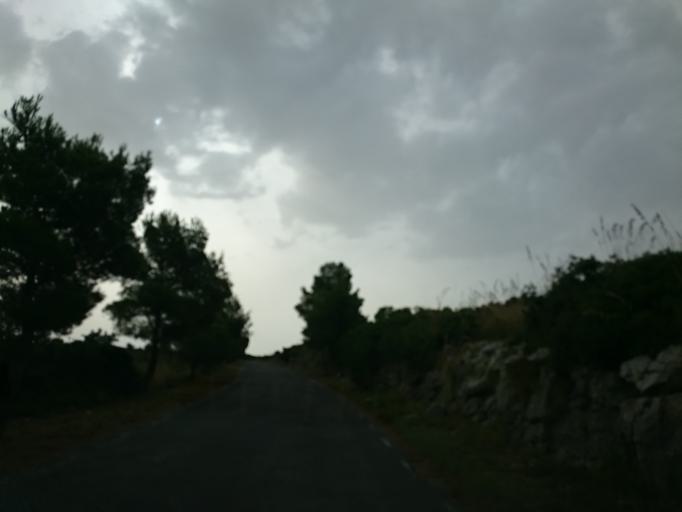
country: ES
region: Catalonia
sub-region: Provincia de Barcelona
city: Begues
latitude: 41.2801
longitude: 1.8823
